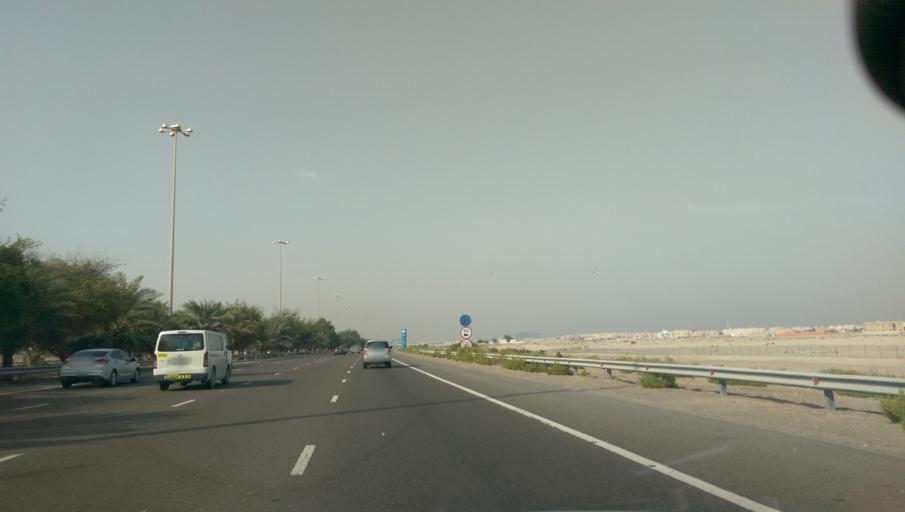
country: AE
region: Abu Dhabi
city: Abu Dhabi
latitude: 24.3620
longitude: 54.6505
